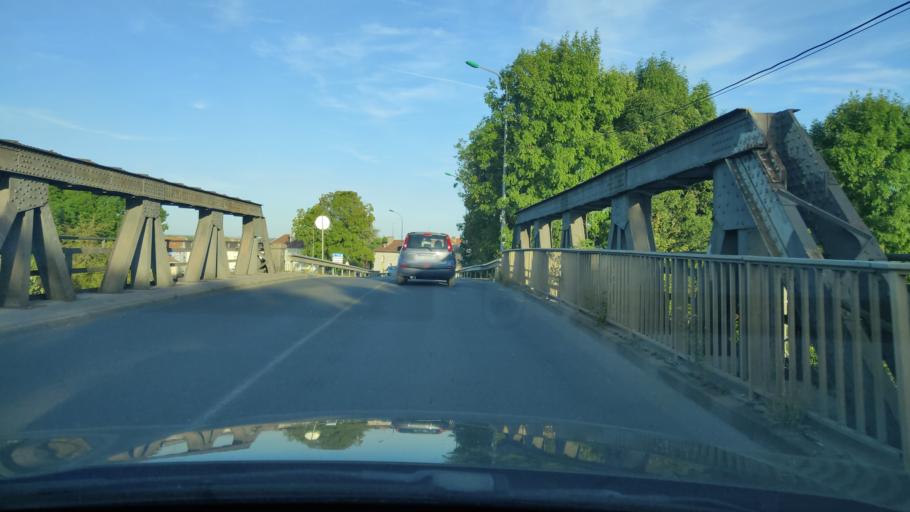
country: FR
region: Lorraine
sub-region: Departement de la Moselle
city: Maizieres-les-Metz
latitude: 49.2107
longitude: 6.1574
